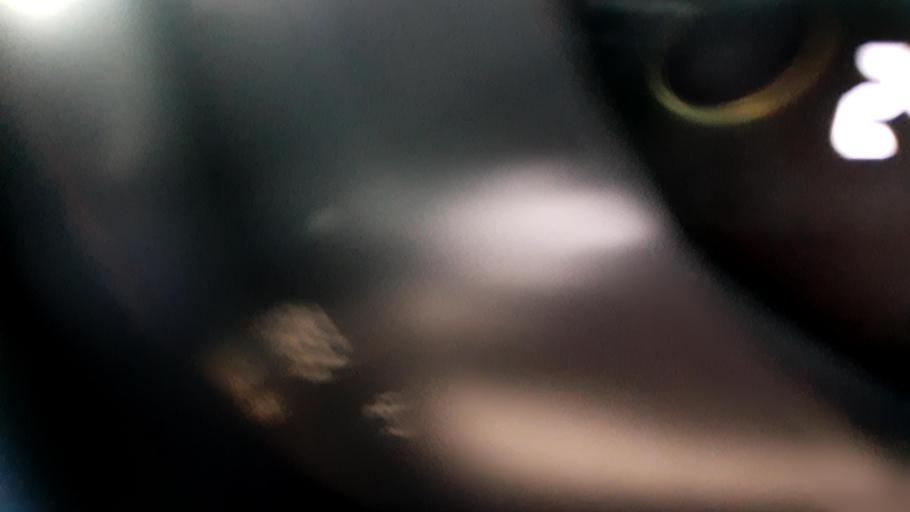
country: RU
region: Nizjnij Novgorod
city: Bor
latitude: 56.3606
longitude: 44.0762
